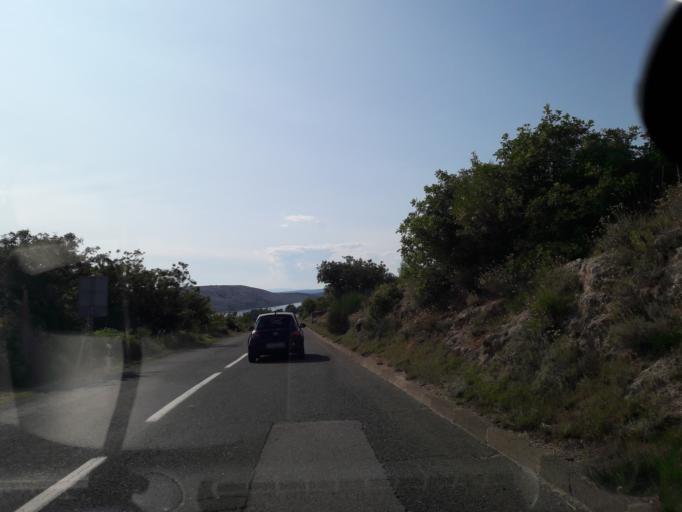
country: HR
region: Primorsko-Goranska
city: Banjol
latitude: 44.7073
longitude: 14.8368
